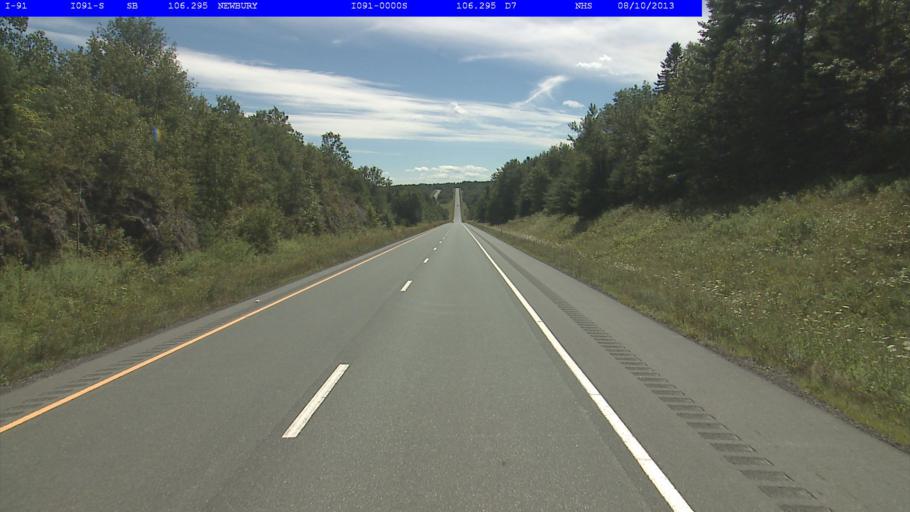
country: US
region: New Hampshire
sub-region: Grafton County
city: Haverhill
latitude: 44.1046
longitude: -72.1091
